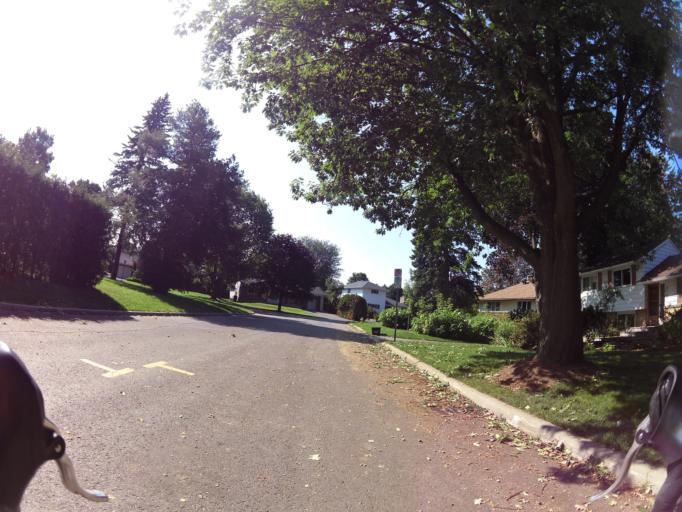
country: CA
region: Ontario
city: Ottawa
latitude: 45.3953
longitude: -75.6669
